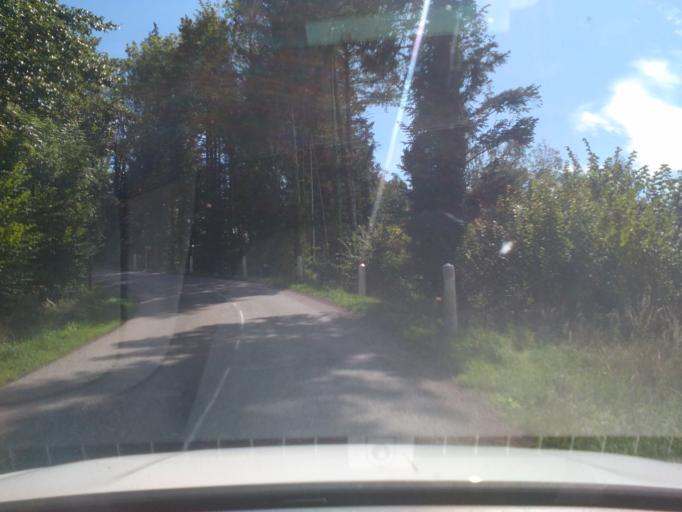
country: FR
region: Lorraine
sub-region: Departement des Vosges
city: Senones
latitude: 48.3816
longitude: 6.9622
